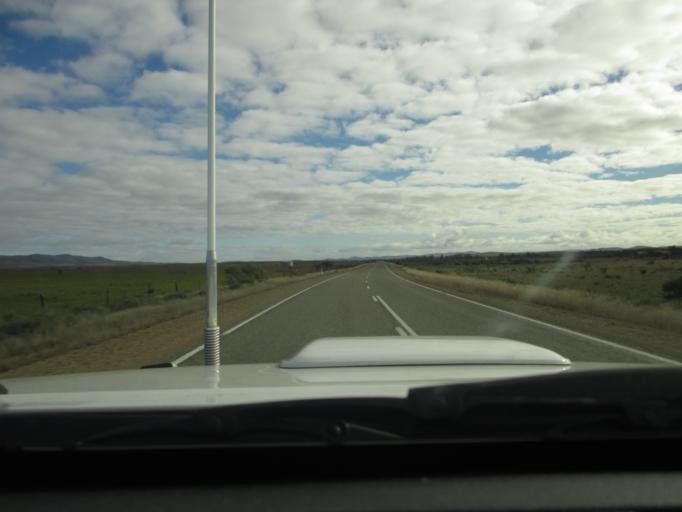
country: AU
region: South Australia
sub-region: Flinders Ranges
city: Quorn
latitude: -32.4122
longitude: 138.5207
